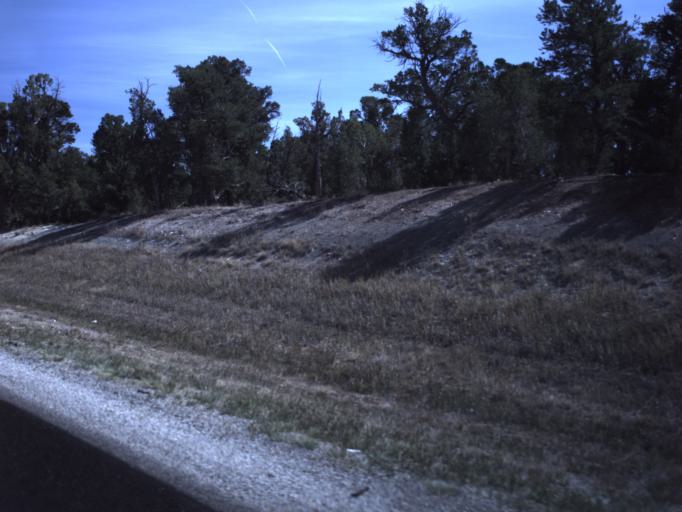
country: US
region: Colorado
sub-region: Dolores County
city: Dove Creek
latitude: 37.8261
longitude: -109.0756
